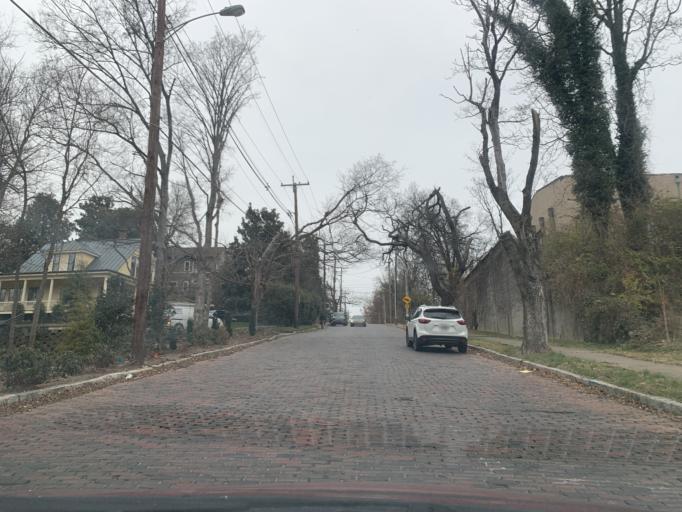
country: US
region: Kentucky
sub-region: Jefferson County
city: Saint Matthews
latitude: 38.2491
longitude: -85.6971
